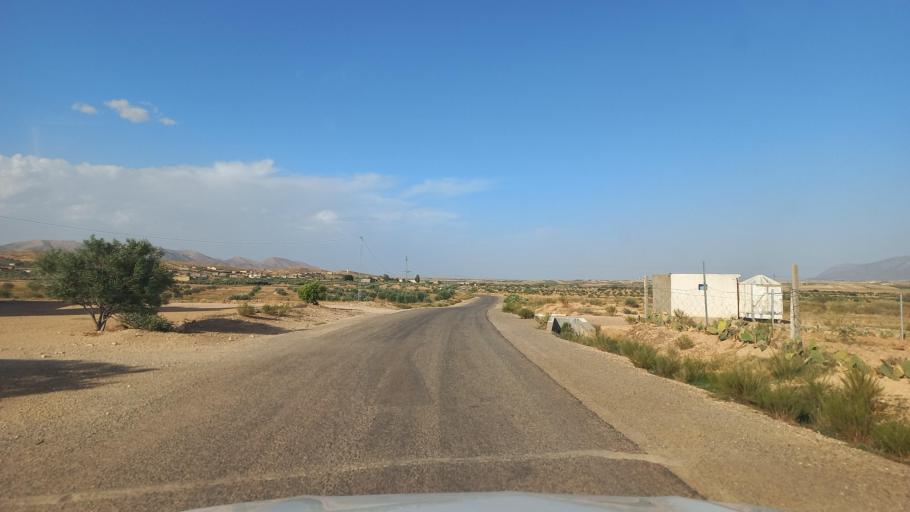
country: TN
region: Al Qasrayn
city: Sbiba
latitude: 35.3686
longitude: 9.0094
